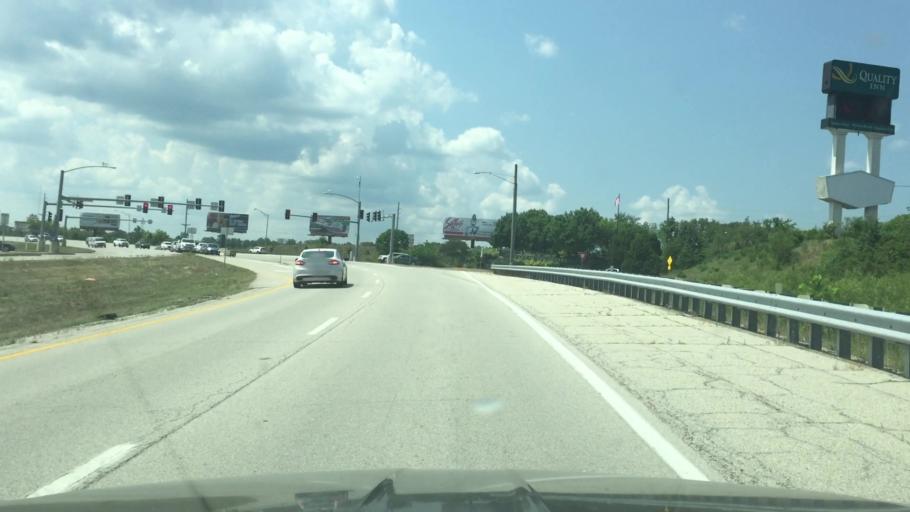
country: US
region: Missouri
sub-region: Miller County
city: Lake Ozark
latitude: 38.1765
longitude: -92.6150
